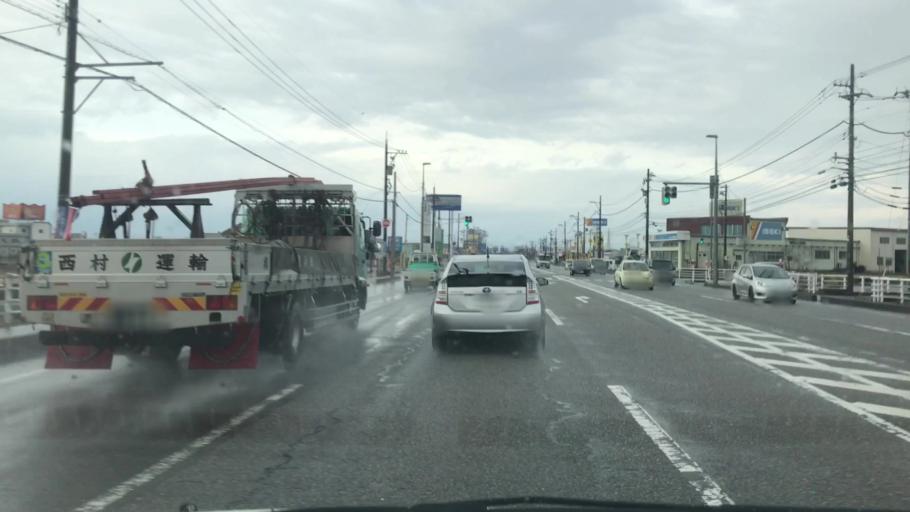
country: JP
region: Toyama
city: Toyama-shi
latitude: 36.6388
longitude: 137.2093
